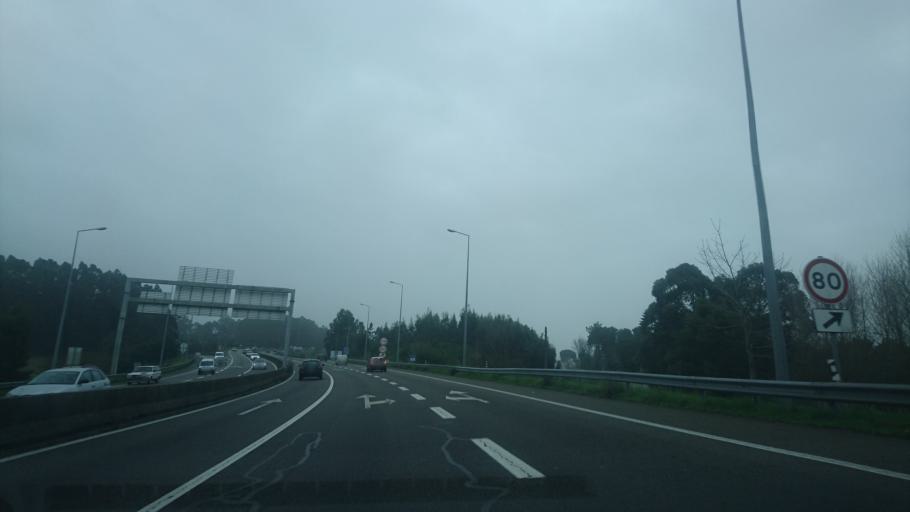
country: PT
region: Porto
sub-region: Vila Nova de Gaia
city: Gulpilhares
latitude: 41.0900
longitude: -8.6310
